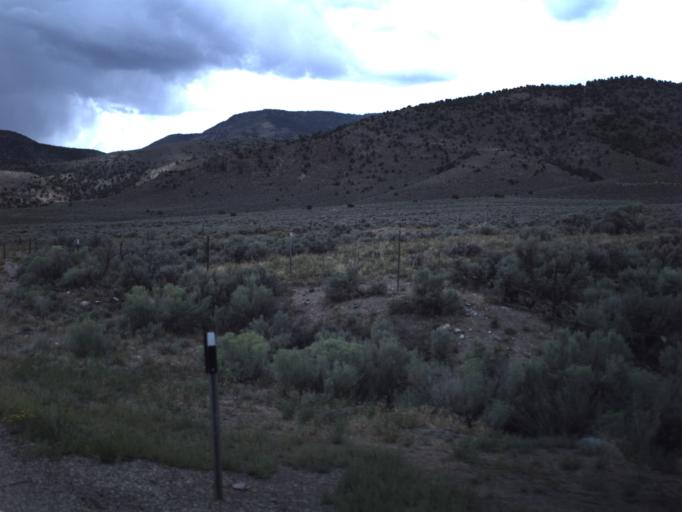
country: US
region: Utah
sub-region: Piute County
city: Junction
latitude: 38.2018
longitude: -112.1748
